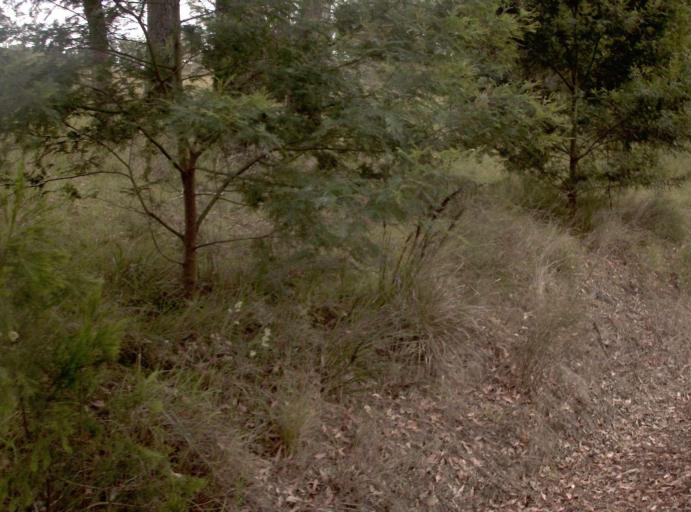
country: AU
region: Victoria
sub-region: East Gippsland
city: Bairnsdale
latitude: -37.7239
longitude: 147.5921
